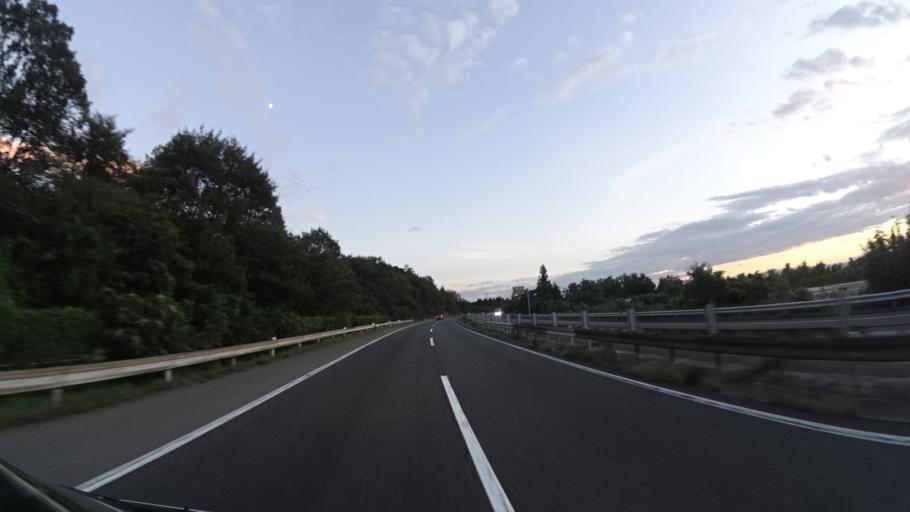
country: JP
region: Shiga Prefecture
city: Youkaichi
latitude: 35.1415
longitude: 136.2810
